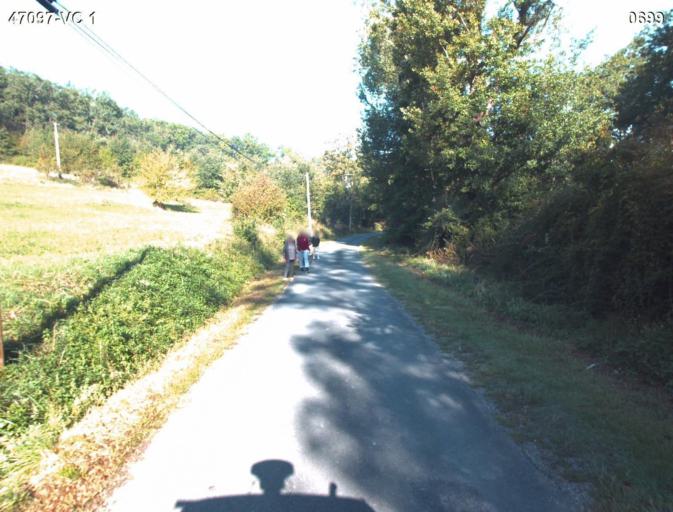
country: FR
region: Aquitaine
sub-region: Departement du Lot-et-Garonne
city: Vianne
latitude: 44.2158
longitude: 0.3494
